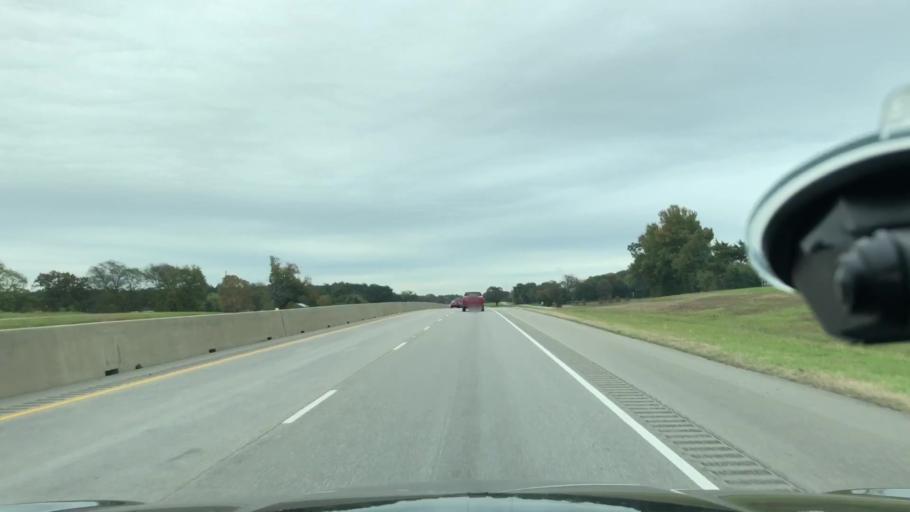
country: US
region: Texas
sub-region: Franklin County
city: Mount Vernon
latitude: 33.1621
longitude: -95.1559
